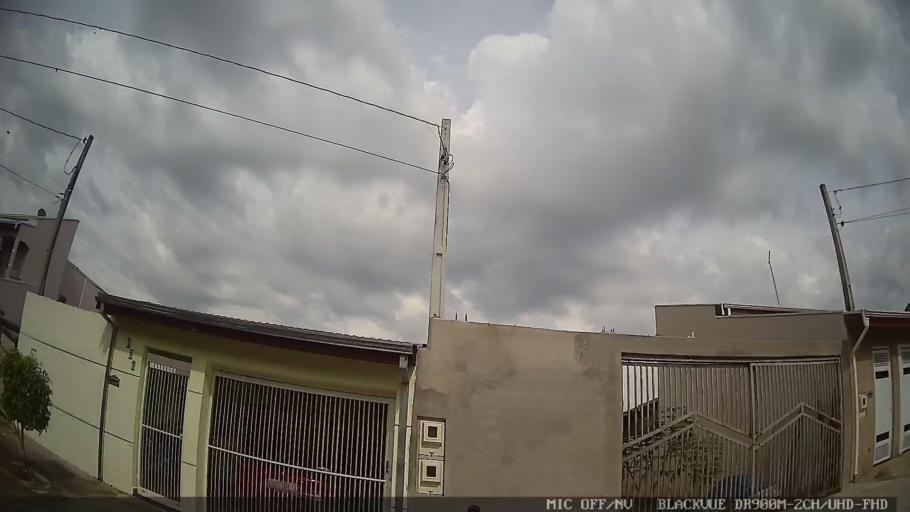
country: BR
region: Sao Paulo
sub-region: Indaiatuba
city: Indaiatuba
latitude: -23.1264
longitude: -47.2499
